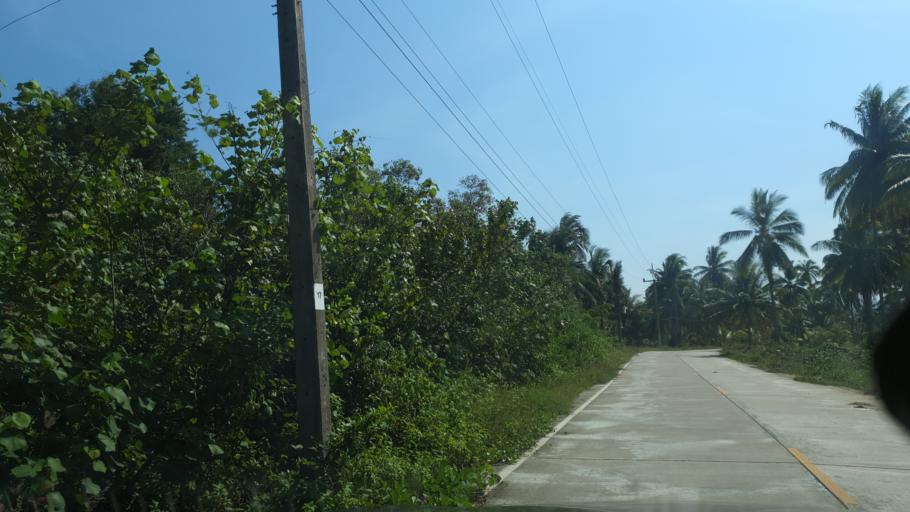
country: TH
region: Surat Thani
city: Tha Chana
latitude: 9.5964
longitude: 99.2053
